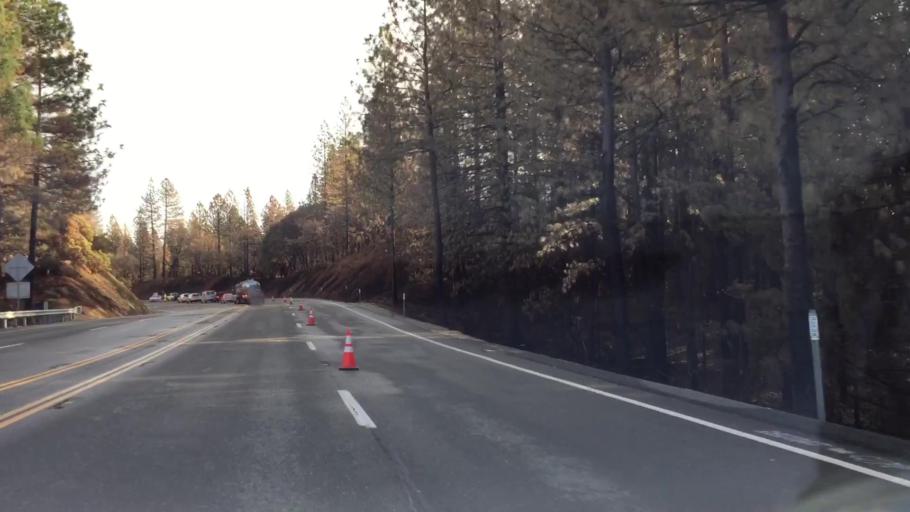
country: US
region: California
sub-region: Butte County
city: Paradise
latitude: 39.7104
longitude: -121.5270
